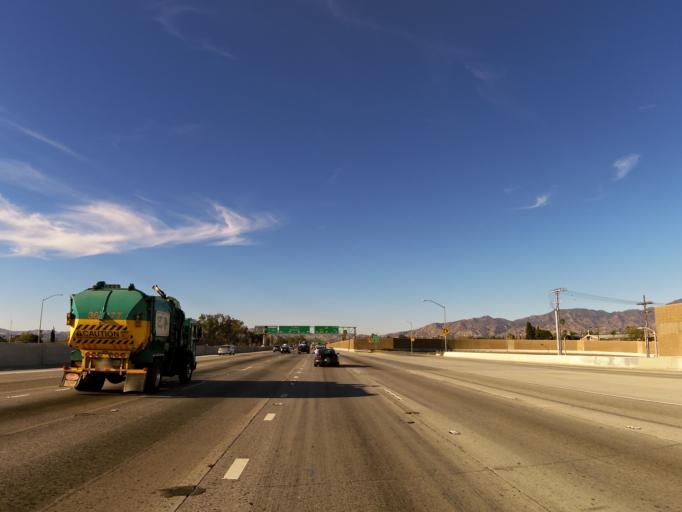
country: US
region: California
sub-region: Los Angeles County
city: San Fernando
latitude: 34.2563
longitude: -118.4344
